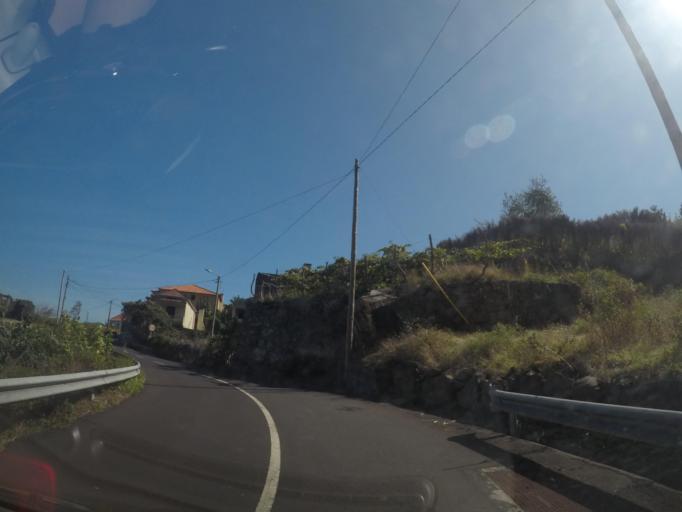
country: PT
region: Madeira
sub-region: Porto Moniz
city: Porto Moniz
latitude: 32.8245
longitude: -17.1135
